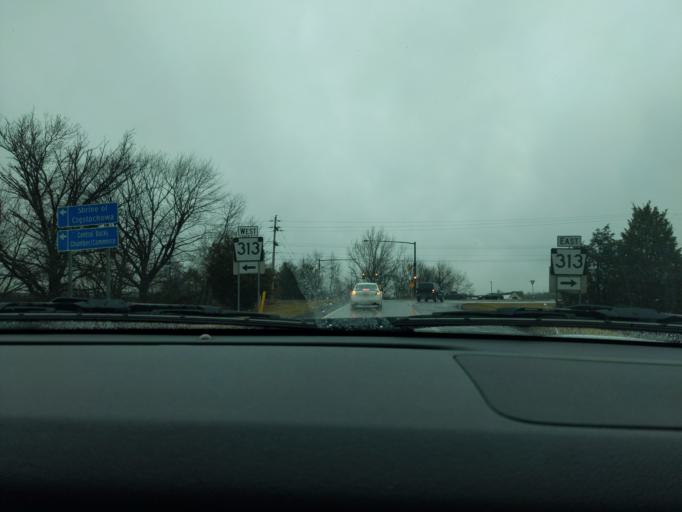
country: US
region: Pennsylvania
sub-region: Bucks County
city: Doylestown
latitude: 40.3306
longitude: -75.1354
